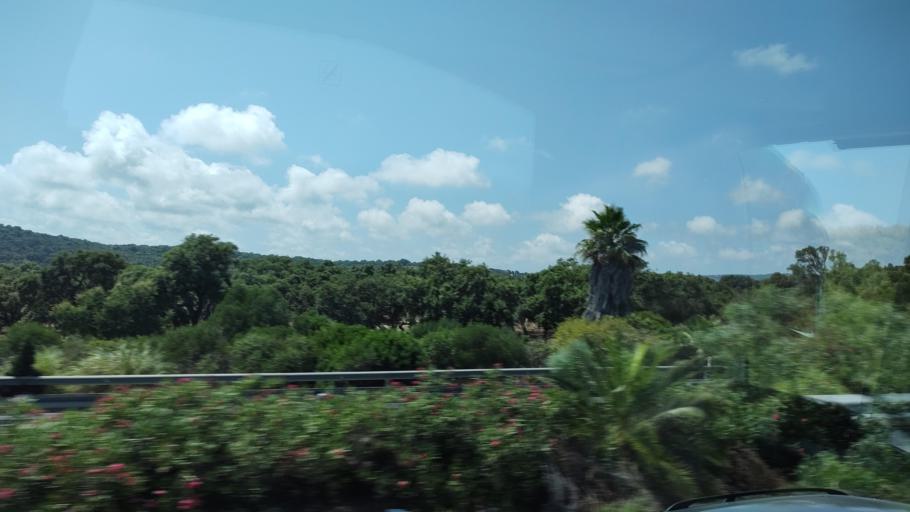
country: ES
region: Andalusia
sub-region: Provincia de Cadiz
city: San Roque
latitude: 36.2661
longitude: -5.3168
